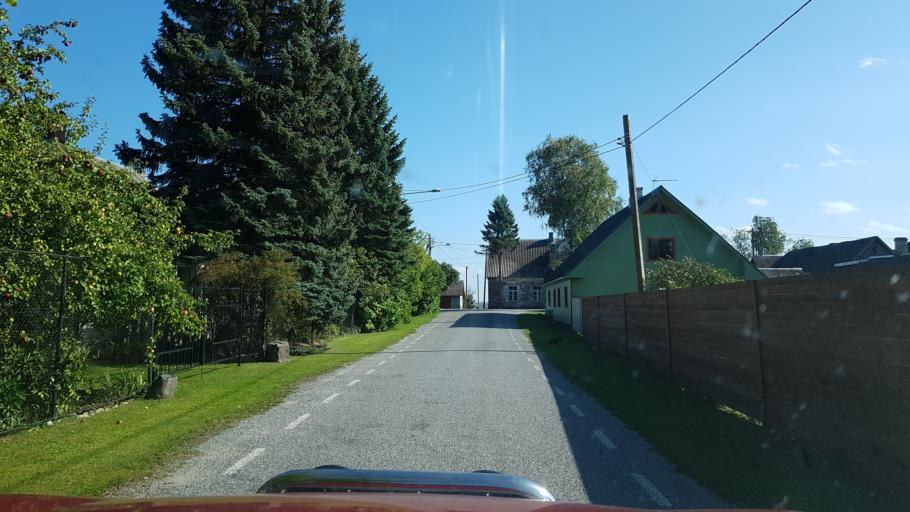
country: EE
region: Polvamaa
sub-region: Raepina vald
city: Rapina
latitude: 58.2335
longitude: 27.4735
